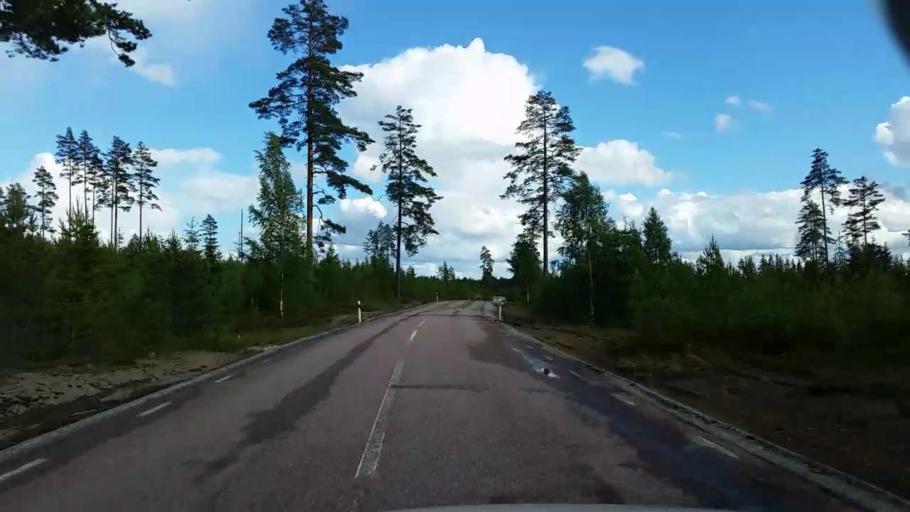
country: SE
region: Vaestmanland
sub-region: Fagersta Kommun
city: Fagersta
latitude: 59.8940
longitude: 15.8217
